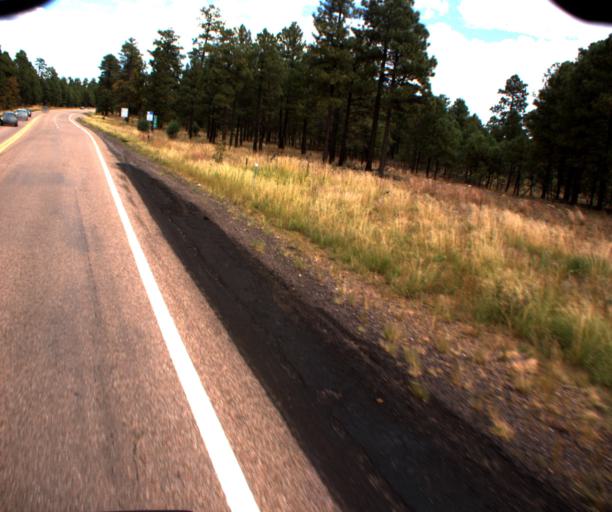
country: US
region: Arizona
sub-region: Navajo County
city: Heber-Overgaard
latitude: 34.3571
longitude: -110.6957
